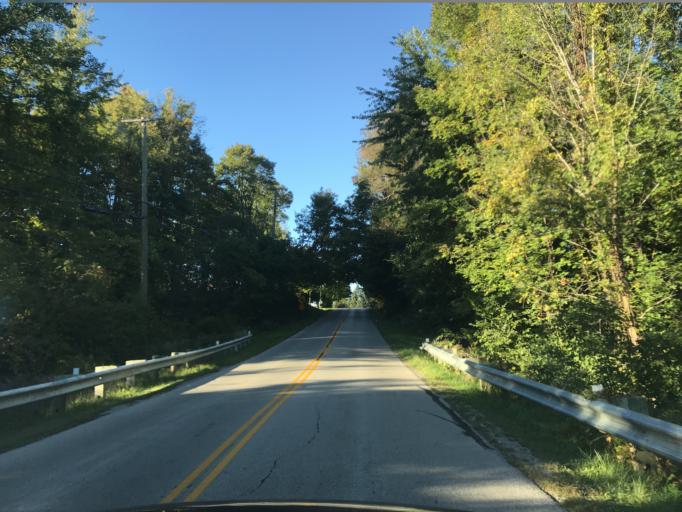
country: US
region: Ohio
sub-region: Ashtabula County
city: Edgewood
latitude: 41.8498
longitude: -80.7563
